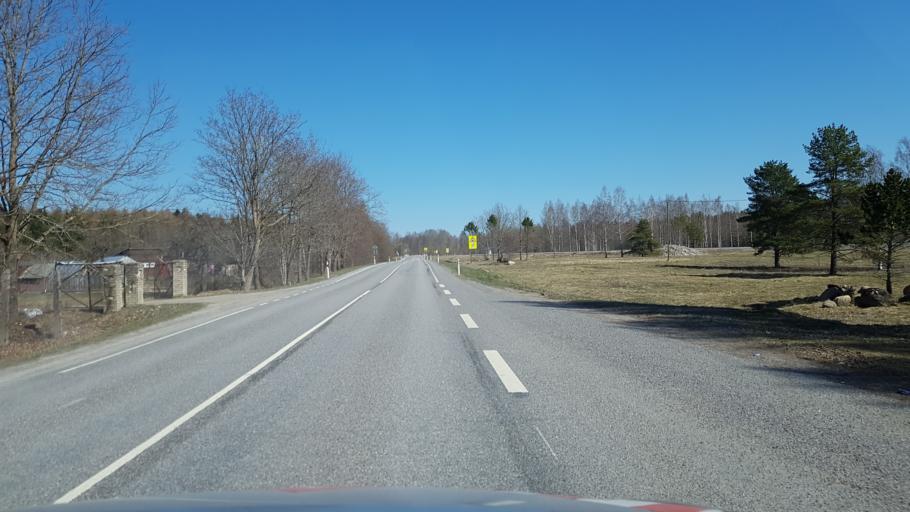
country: EE
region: Ida-Virumaa
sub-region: Kohtla-Jaerve linn
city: Kohtla-Jarve
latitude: 59.3276
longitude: 27.2687
